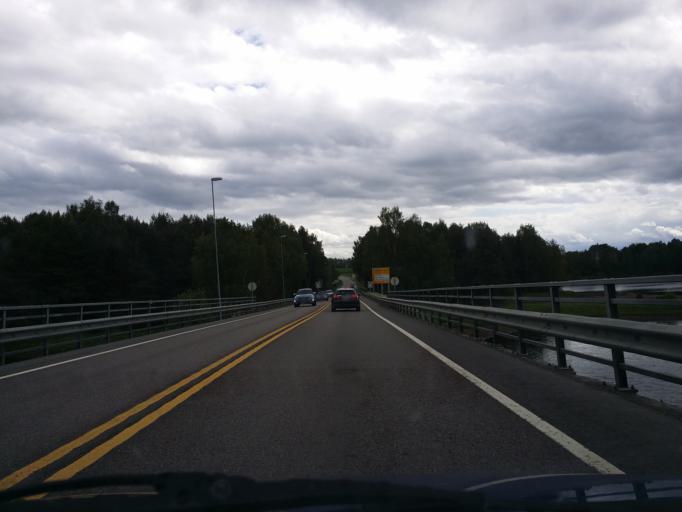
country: NO
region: Hedmark
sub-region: Hamar
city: Hamar
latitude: 60.7948
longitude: 11.1226
